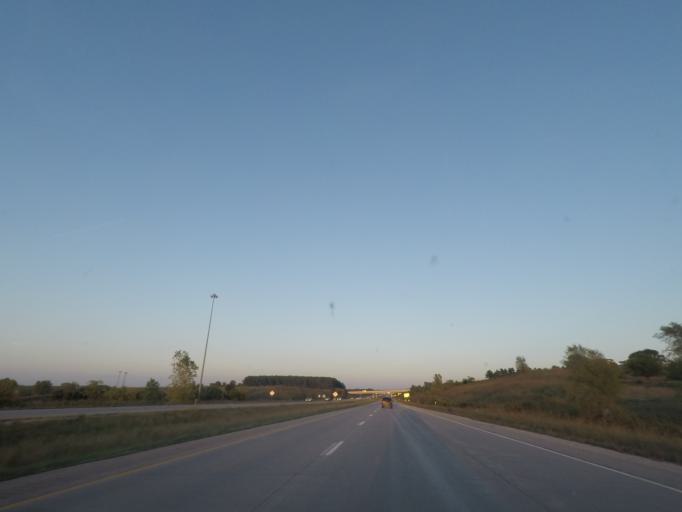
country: US
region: Iowa
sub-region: Polk County
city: West Des Moines
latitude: 41.5226
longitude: -93.7670
